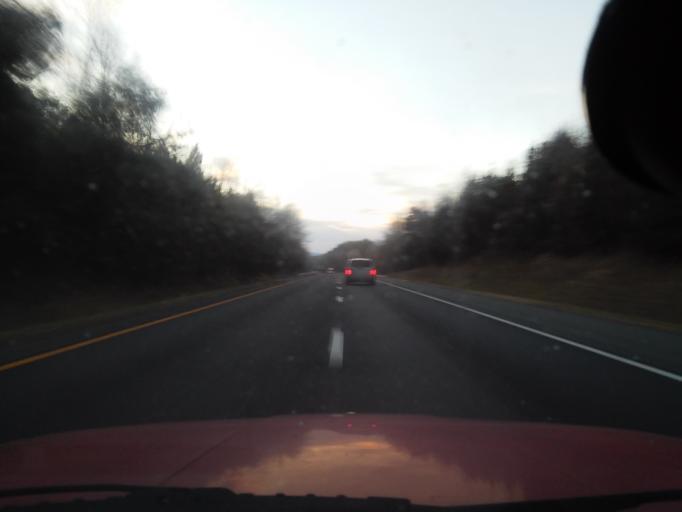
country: US
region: Virginia
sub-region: Fluvanna County
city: Lake Monticello
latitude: 38.0108
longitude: -78.3752
